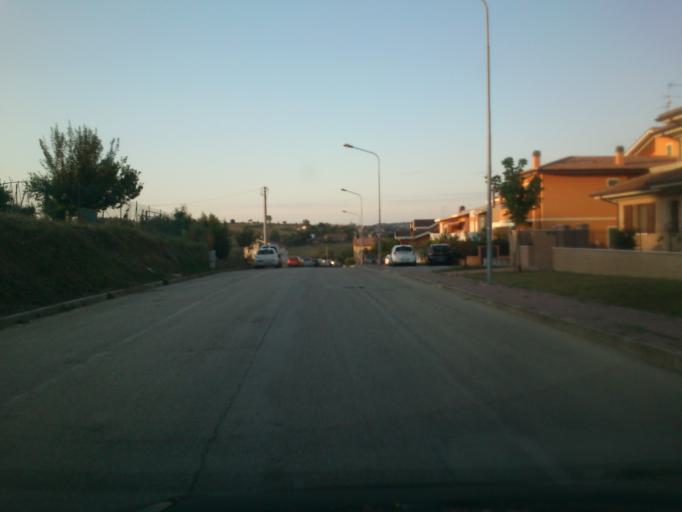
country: IT
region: The Marches
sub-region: Provincia di Pesaro e Urbino
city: Lucrezia
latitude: 43.7715
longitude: 12.9229
